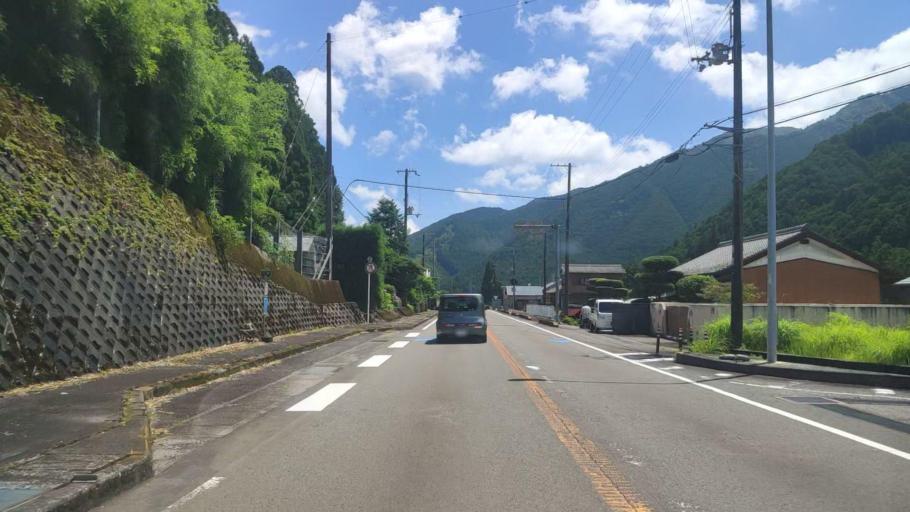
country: JP
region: Mie
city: Owase
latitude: 33.9798
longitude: 136.1049
